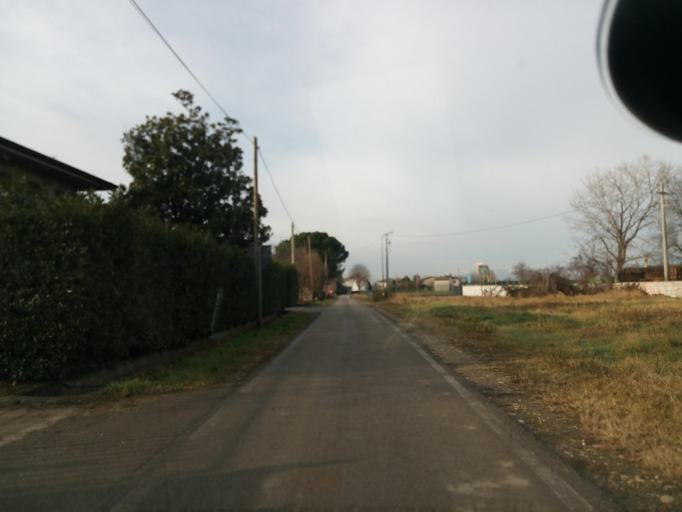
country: IT
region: Veneto
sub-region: Provincia di Treviso
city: Trevignano
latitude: 45.7474
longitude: 12.0518
